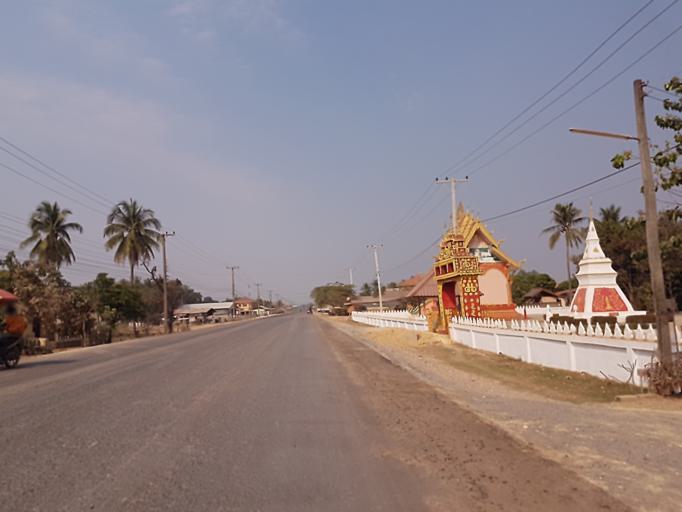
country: TH
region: Nong Khai
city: Nong Khai
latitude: 17.9166
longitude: 102.7658
